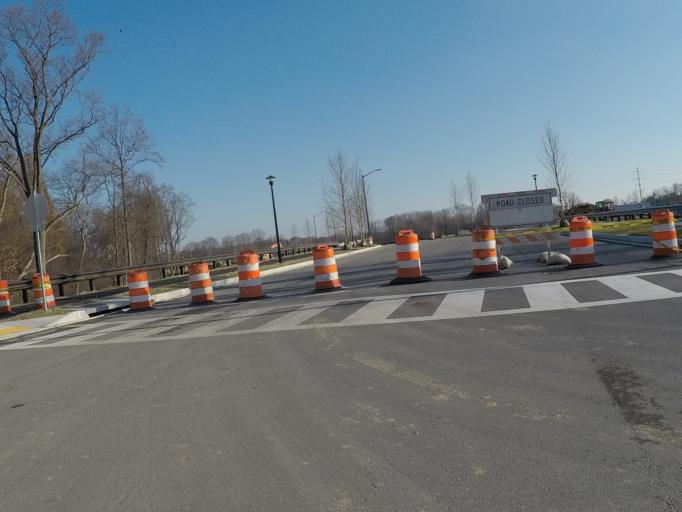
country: US
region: Maryland
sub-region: Howard County
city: Riverside
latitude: 39.2079
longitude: -76.8643
